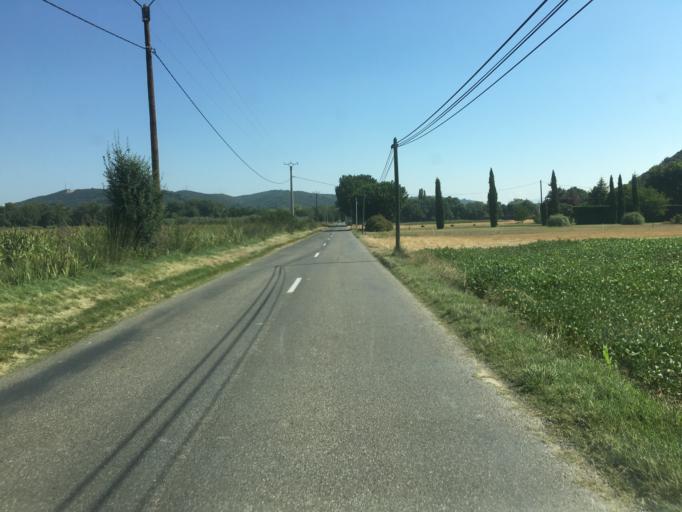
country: FR
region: Provence-Alpes-Cote d'Azur
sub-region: Departement des Alpes-de-Haute-Provence
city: Oraison
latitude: 43.8748
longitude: 5.9051
